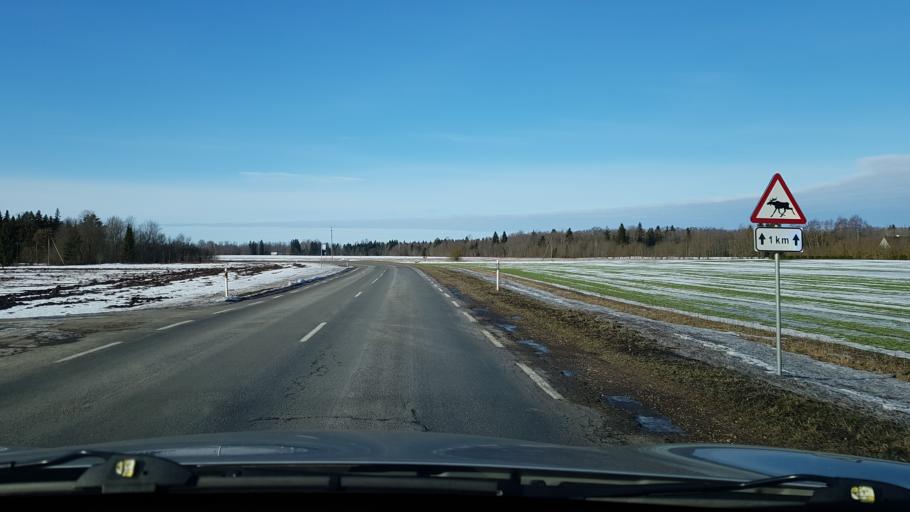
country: EE
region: Viljandimaa
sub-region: Vohma linn
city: Vohma
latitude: 58.6391
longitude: 25.6756
